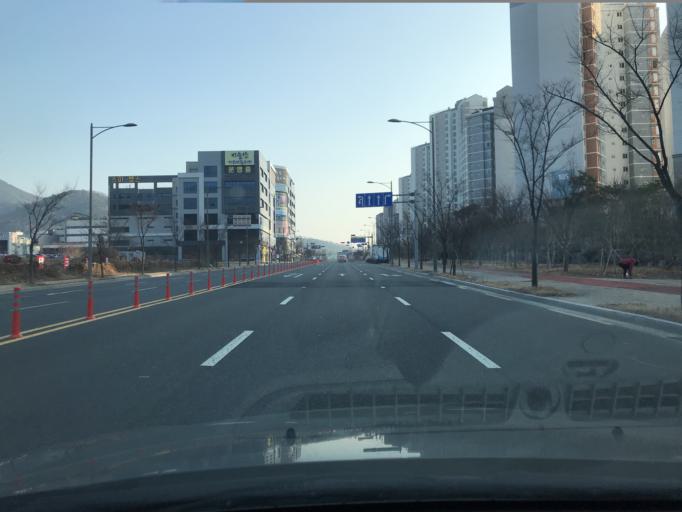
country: KR
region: Daegu
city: Hwawon
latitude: 35.6957
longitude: 128.4698
